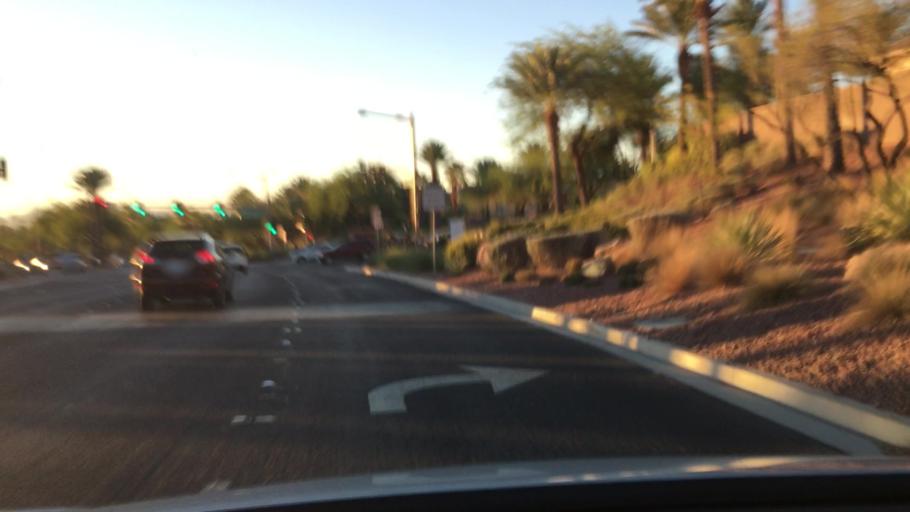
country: US
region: Nevada
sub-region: Clark County
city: Summerlin South
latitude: 36.1462
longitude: -115.3415
